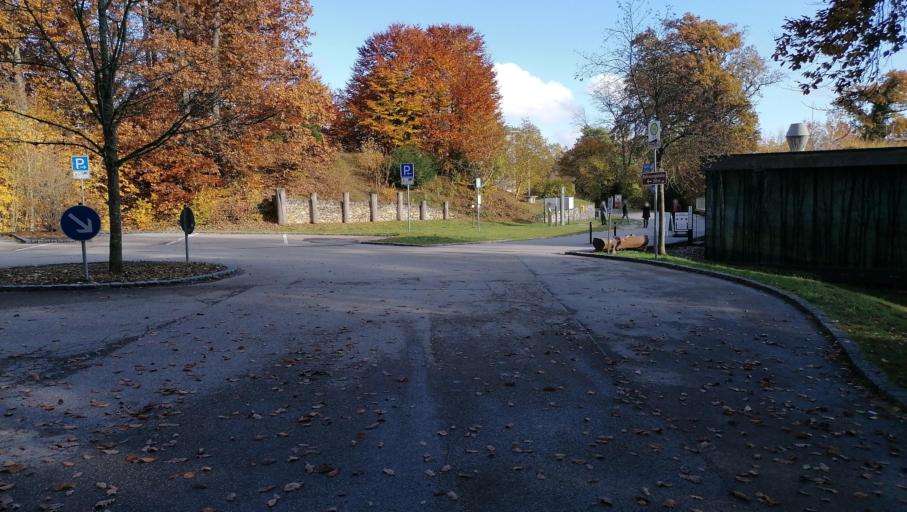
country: DE
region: Bavaria
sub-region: Lower Bavaria
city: Ihrlerstein
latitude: 48.9184
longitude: 11.8554
